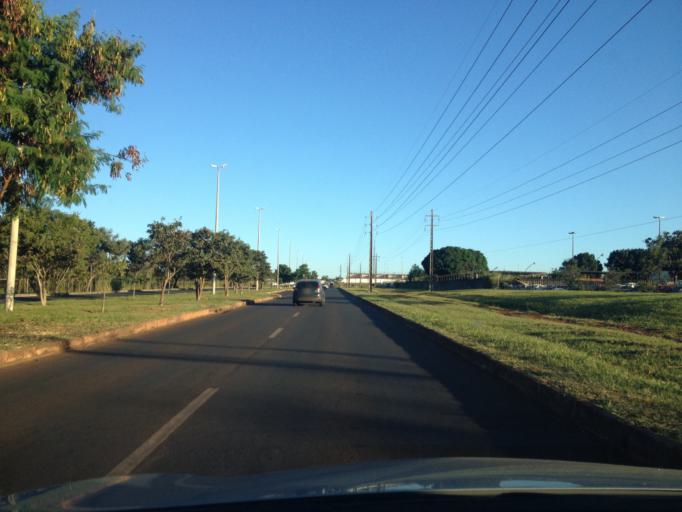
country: BR
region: Federal District
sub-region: Brasilia
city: Brasilia
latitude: -15.7681
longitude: -47.8986
